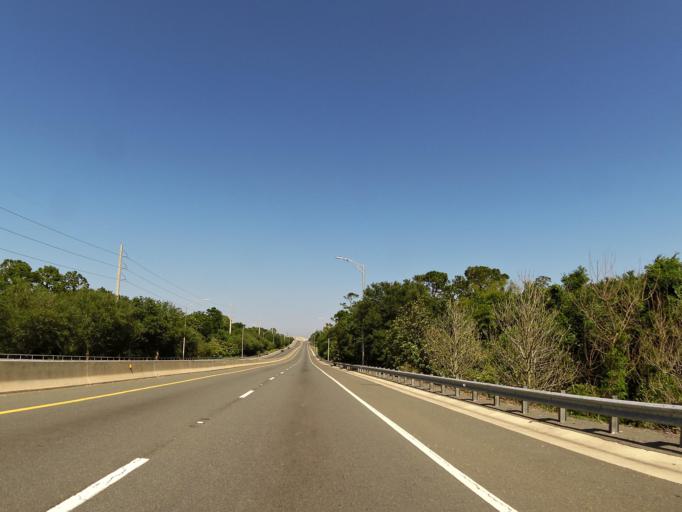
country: US
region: Florida
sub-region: Duval County
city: Atlantic Beach
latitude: 30.3590
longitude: -81.4581
